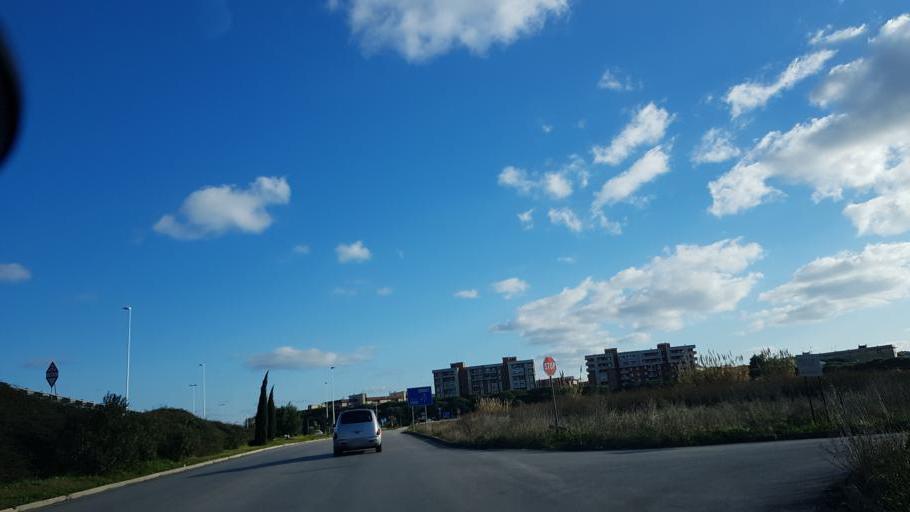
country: IT
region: Apulia
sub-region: Provincia di Brindisi
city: Brindisi
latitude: 40.6246
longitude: 17.9207
